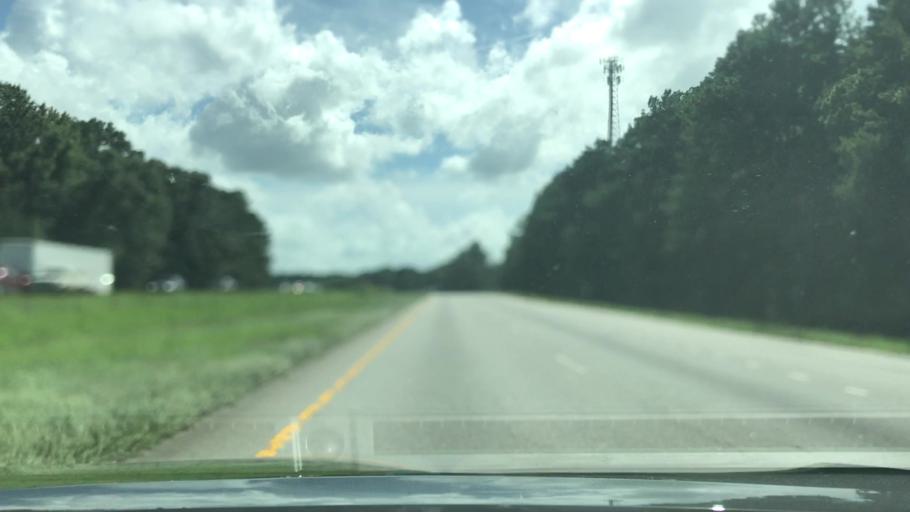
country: US
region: South Carolina
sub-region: Jasper County
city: Ridgeland
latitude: 32.5766
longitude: -80.9338
